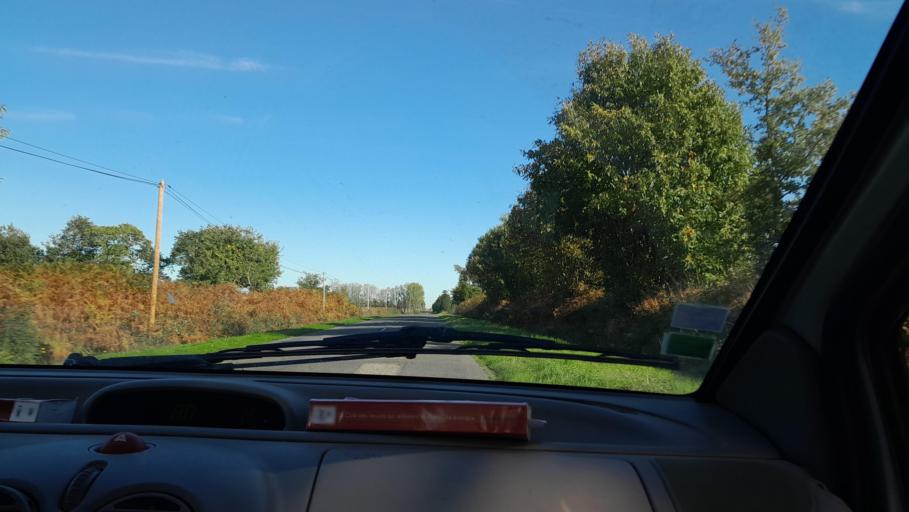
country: FR
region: Brittany
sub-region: Departement d'Ille-et-Vilaine
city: Le Pertre
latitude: 47.9674
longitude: -1.0706
